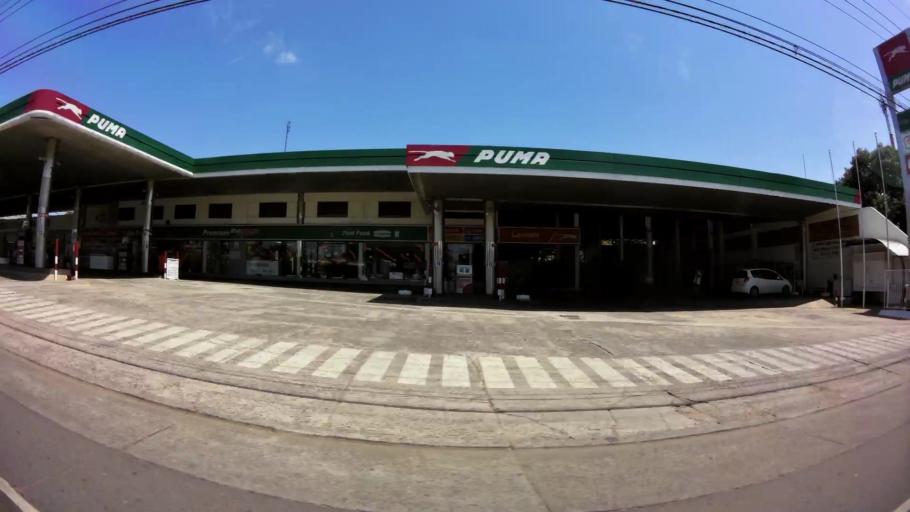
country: PY
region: Central
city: Nemby
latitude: -25.4013
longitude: -57.5435
